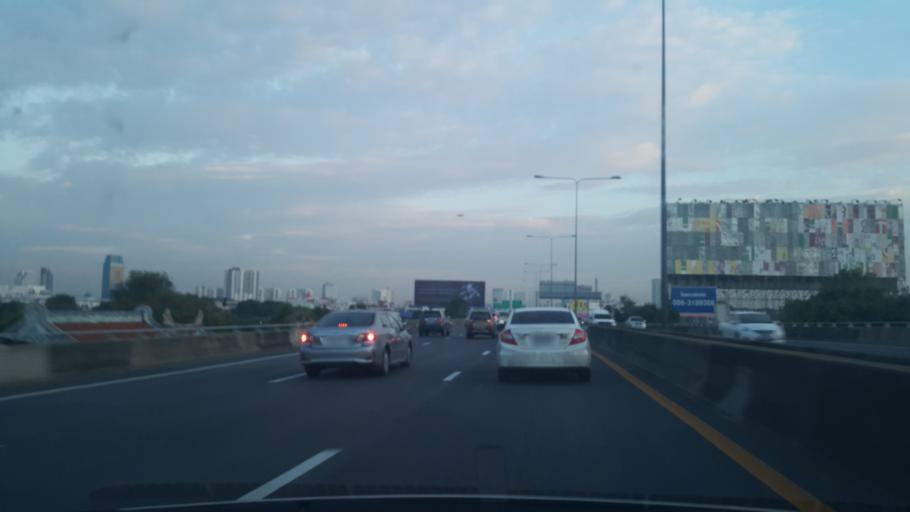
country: TH
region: Bangkok
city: Sathon
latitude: 13.6987
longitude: 100.5211
